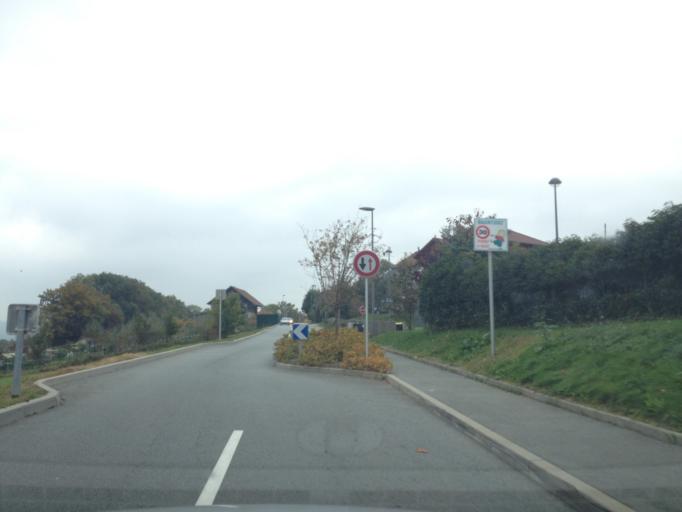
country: FR
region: Rhone-Alpes
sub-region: Departement de la Haute-Savoie
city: Seynod
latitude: 45.8769
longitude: 6.0838
